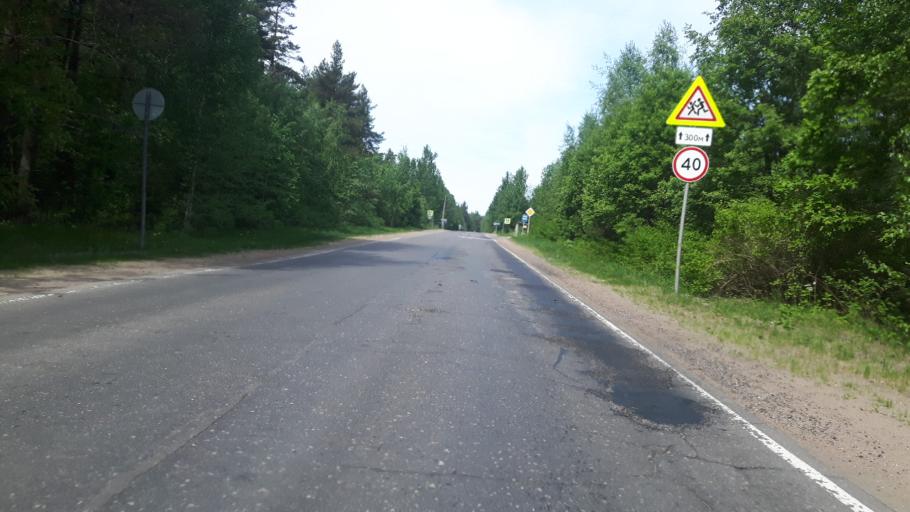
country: RU
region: Leningrad
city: Ust'-Luga
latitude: 59.6446
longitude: 28.2701
